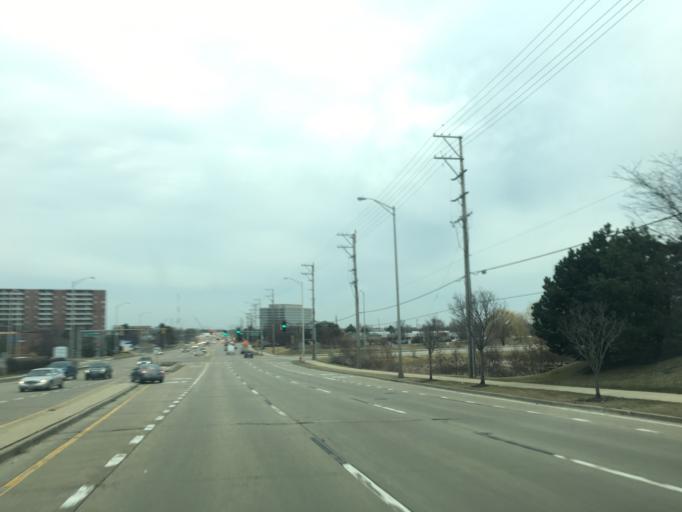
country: US
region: Illinois
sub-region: Cook County
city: Hoffman Estates
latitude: 42.0543
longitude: -88.0796
